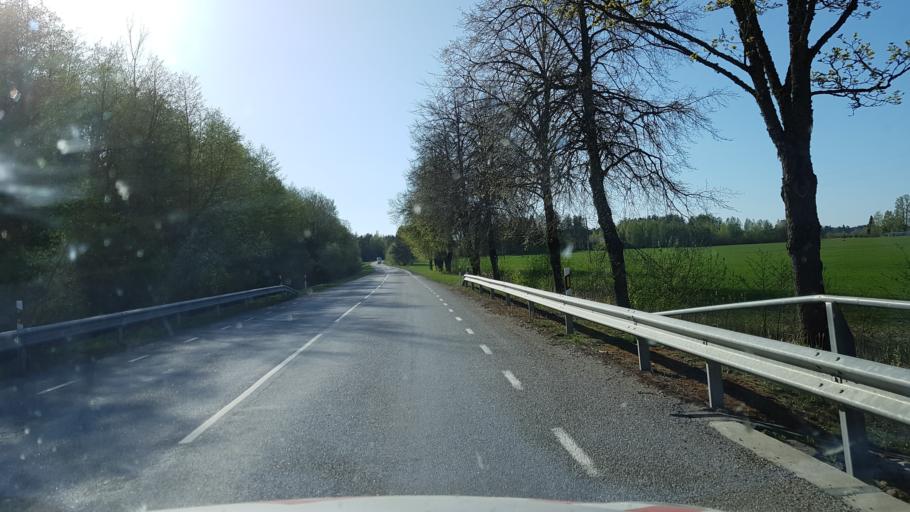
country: EE
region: Paernumaa
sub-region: Sindi linn
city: Sindi
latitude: 58.3434
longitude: 24.6883
